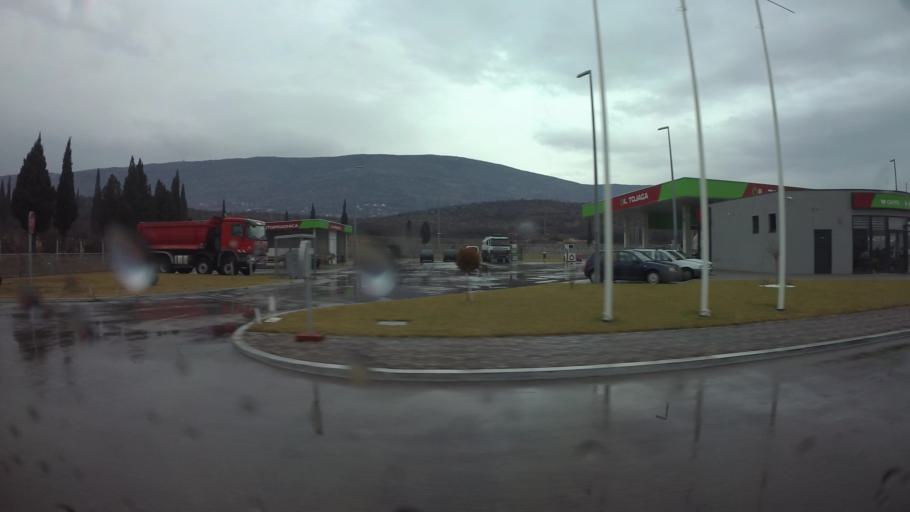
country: BA
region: Federation of Bosnia and Herzegovina
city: Rodoc
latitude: 43.2908
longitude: 17.8467
